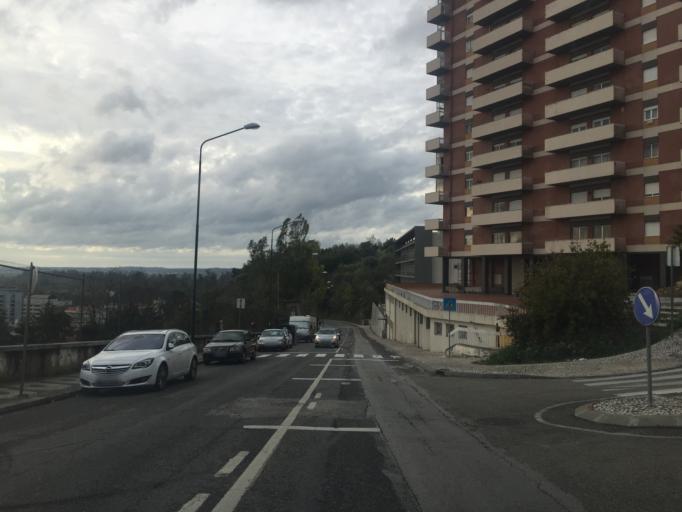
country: PT
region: Coimbra
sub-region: Coimbra
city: Coimbra
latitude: 40.2147
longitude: -8.4303
